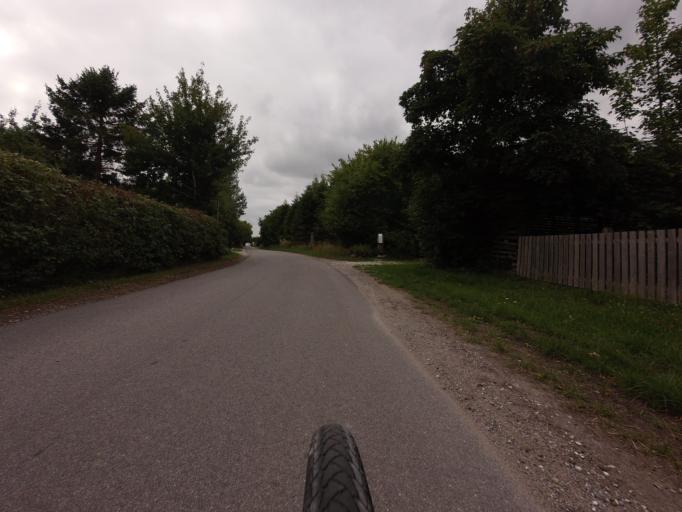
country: DK
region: Zealand
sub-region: Stevns Kommune
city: Store Heddinge
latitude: 55.3410
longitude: 12.4132
